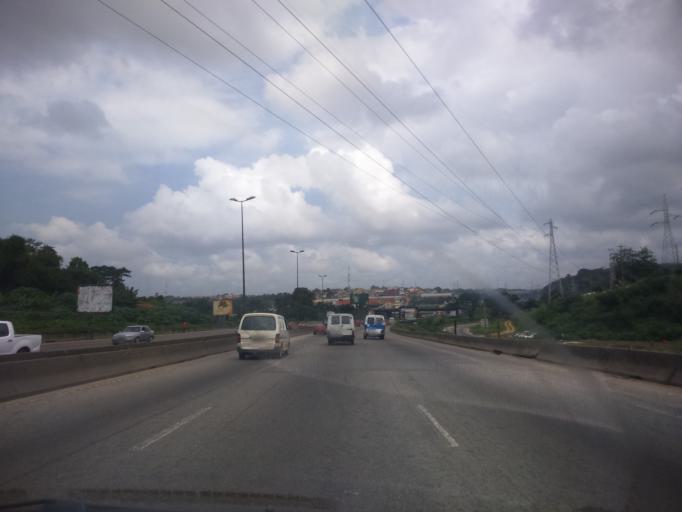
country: CI
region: Lagunes
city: Abidjan
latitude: 5.3613
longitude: -4.0382
